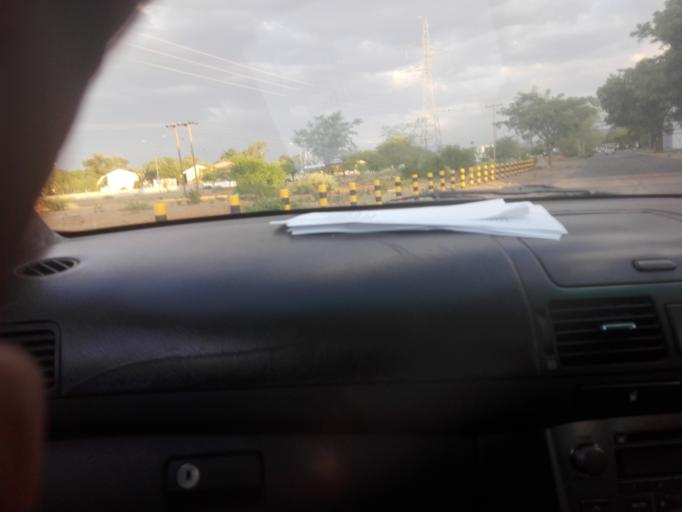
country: BW
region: South East
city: Gaborone
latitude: -24.6846
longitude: 25.8794
